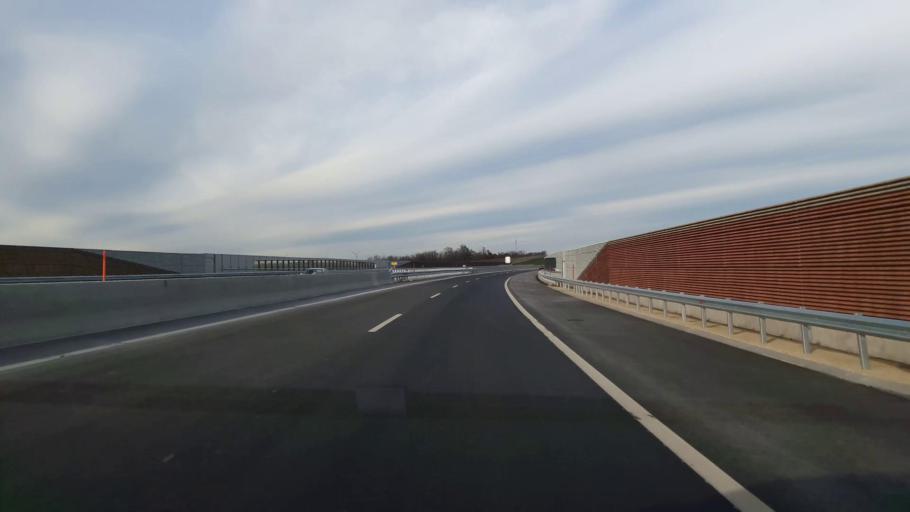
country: AT
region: Lower Austria
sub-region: Politischer Bezirk Mistelbach
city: Wilfersdorf
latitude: 48.5787
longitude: 16.6242
